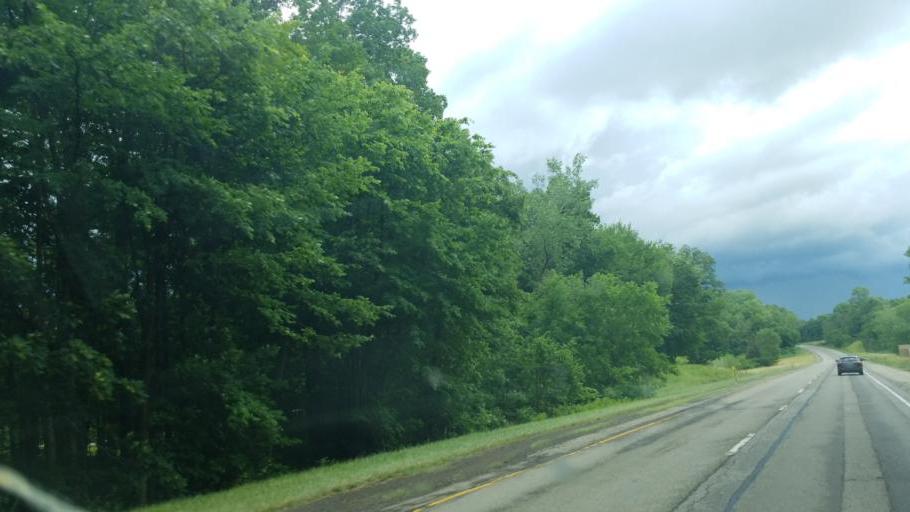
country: US
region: New York
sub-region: Erie County
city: Lake Erie Beach
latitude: 42.5774
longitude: -79.0730
